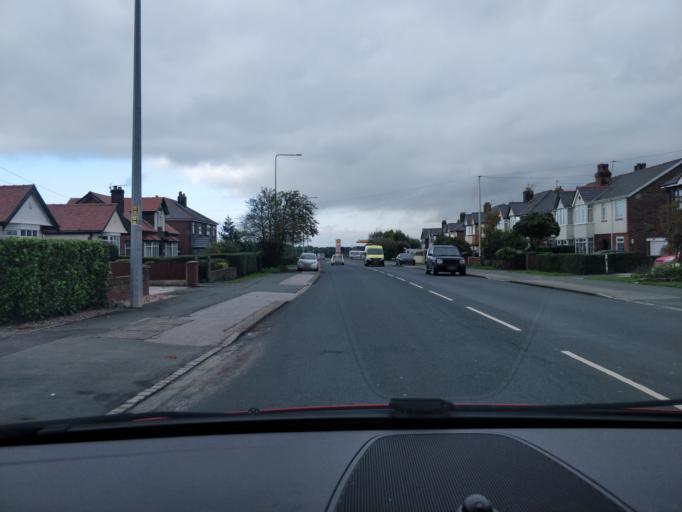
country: GB
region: England
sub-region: Lancashire
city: Ormskirk
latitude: 53.5774
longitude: -2.8953
